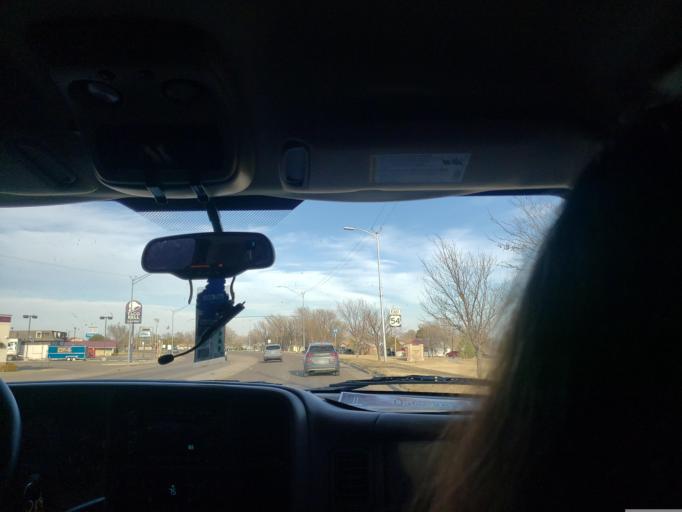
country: US
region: Oklahoma
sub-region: Texas County
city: Guymon
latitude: 36.6795
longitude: -101.4737
